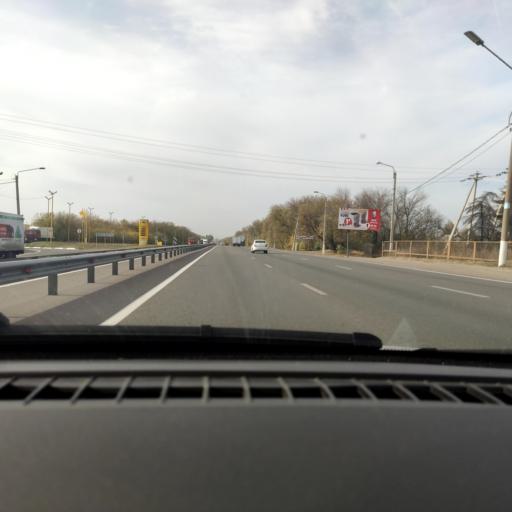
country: RU
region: Voronezj
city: Novaya Usman'
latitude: 51.6186
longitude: 39.3664
